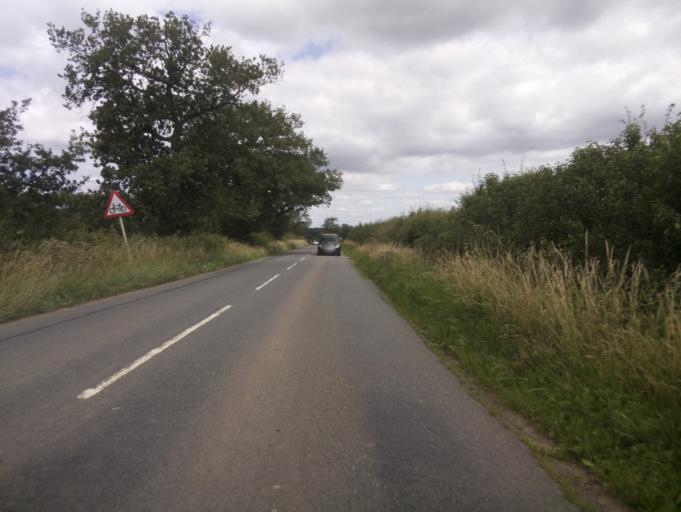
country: GB
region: England
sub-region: Buckinghamshire
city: Newton Longville
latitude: 51.9658
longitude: -0.8165
